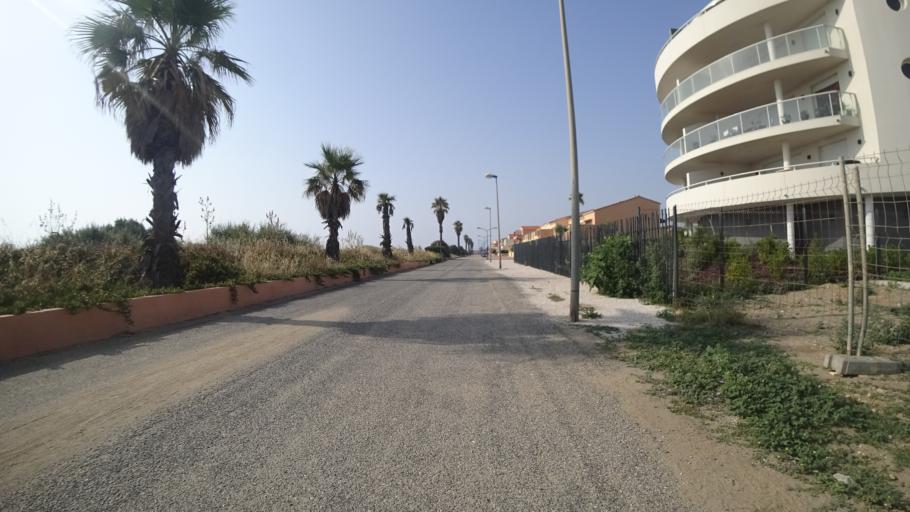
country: FR
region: Languedoc-Roussillon
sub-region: Departement des Pyrenees-Orientales
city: Sainte-Marie-Plage
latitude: 42.7374
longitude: 3.0367
